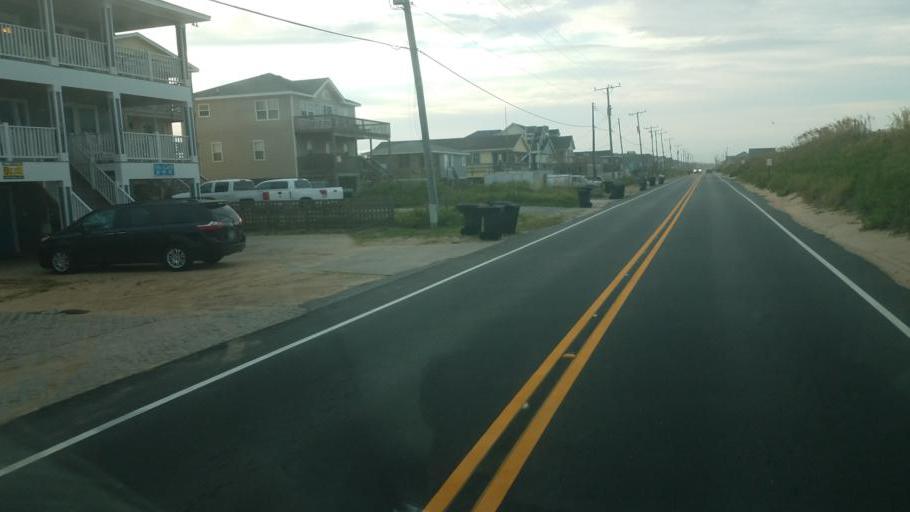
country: US
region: North Carolina
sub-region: Dare County
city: Kitty Hawk
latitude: 36.0713
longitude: -75.6934
